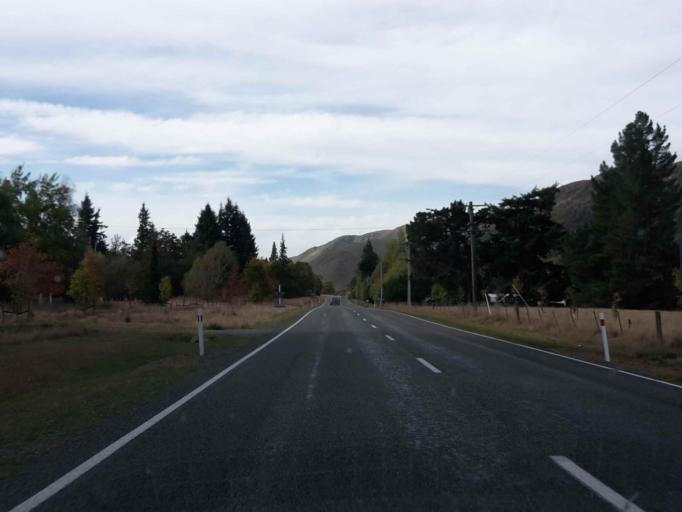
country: NZ
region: Canterbury
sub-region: Timaru District
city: Pleasant Point
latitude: -44.0872
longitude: 170.6553
